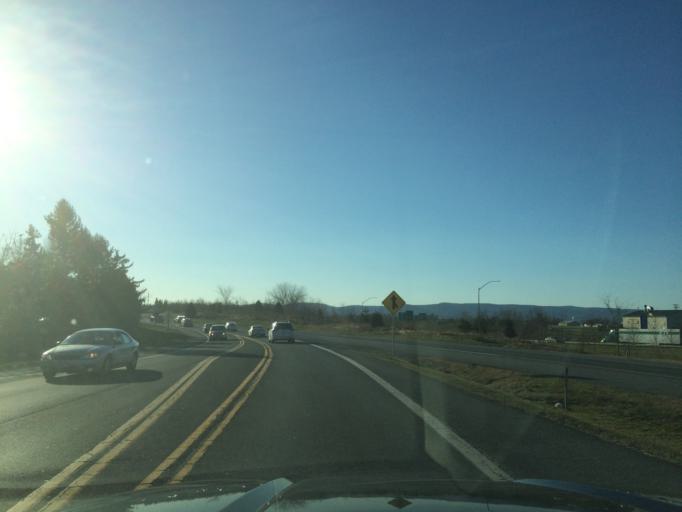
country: US
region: Maryland
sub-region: Frederick County
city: Bartonsville
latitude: 39.4028
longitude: -77.3788
